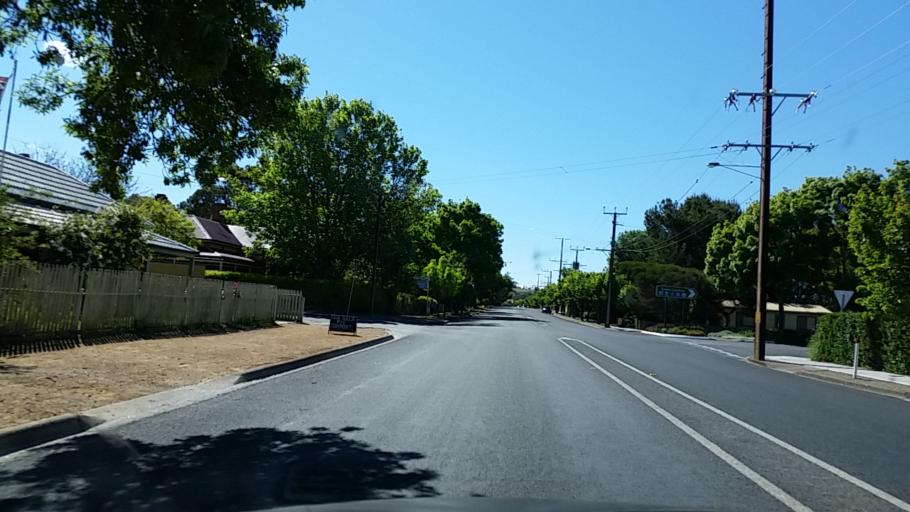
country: AU
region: South Australia
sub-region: Alexandrina
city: Strathalbyn
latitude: -35.2605
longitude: 138.8894
